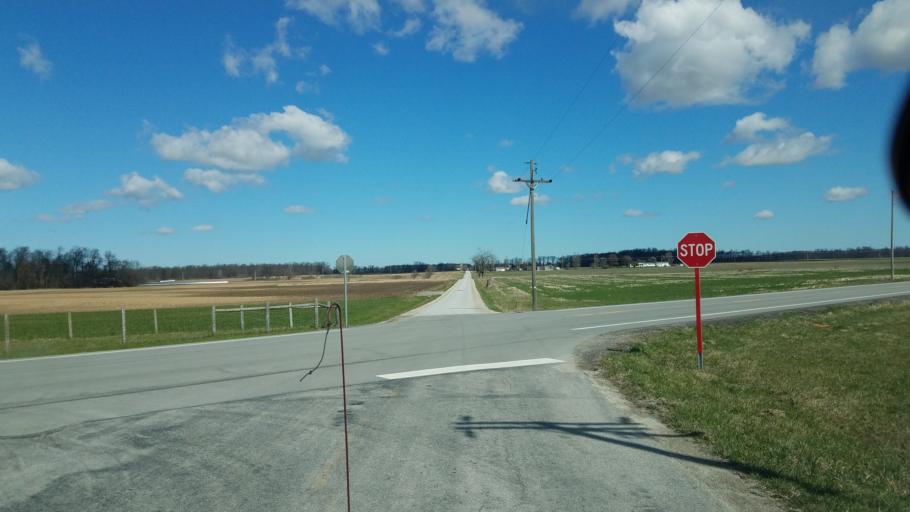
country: US
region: Ohio
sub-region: Sandusky County
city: Mount Carmel
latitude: 41.2062
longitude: -82.9373
